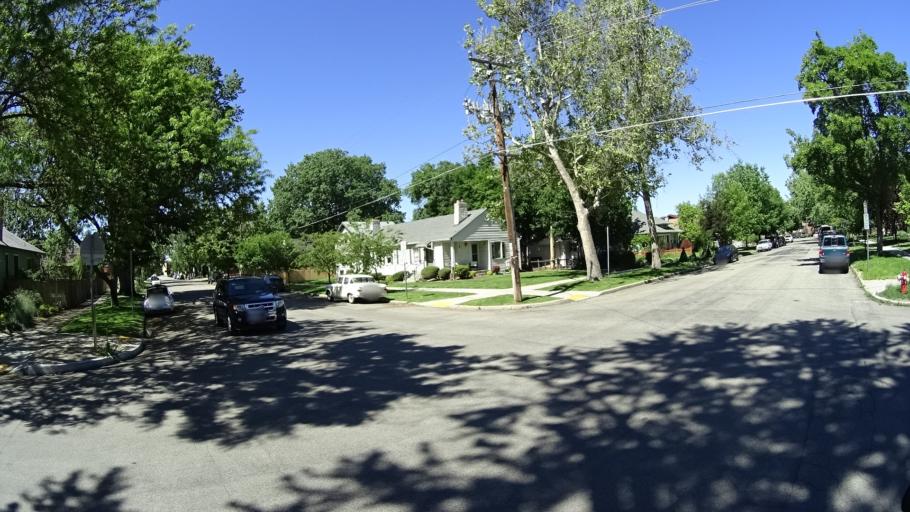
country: US
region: Idaho
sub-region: Ada County
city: Boise
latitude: 43.6238
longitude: -116.2130
